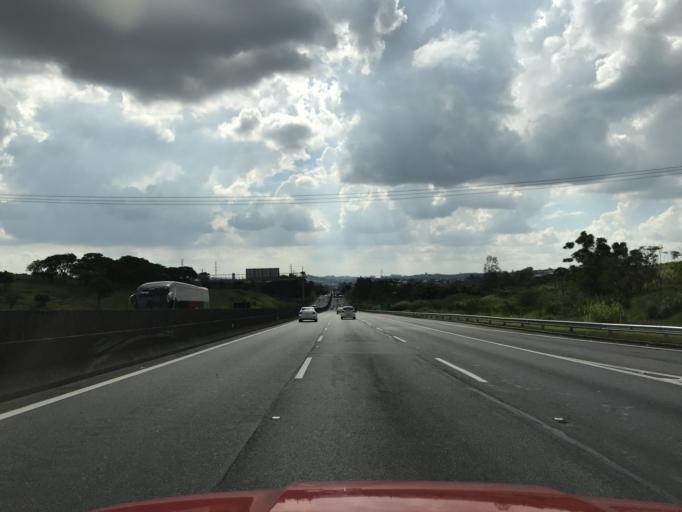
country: BR
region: Sao Paulo
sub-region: Louveira
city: Louveira
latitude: -23.0749
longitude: -46.9834
